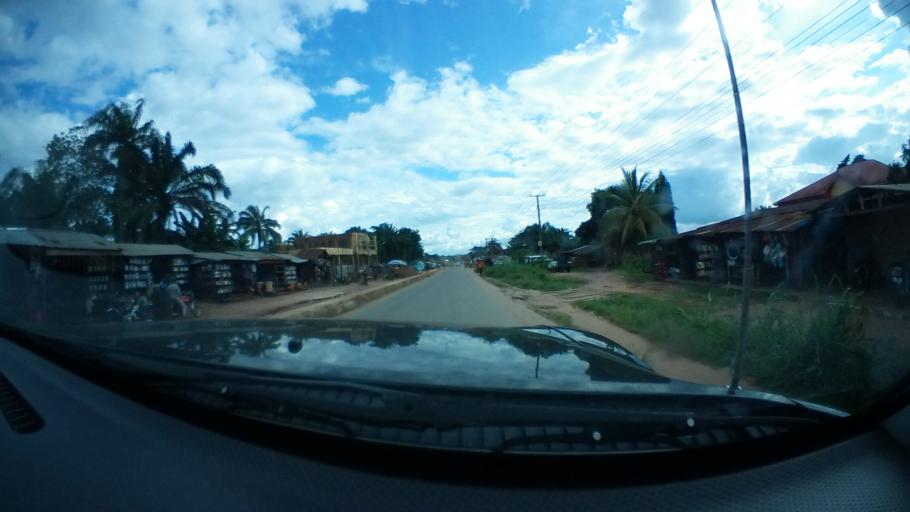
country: NG
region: Anambra
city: Uga
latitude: 5.9080
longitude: 7.1098
